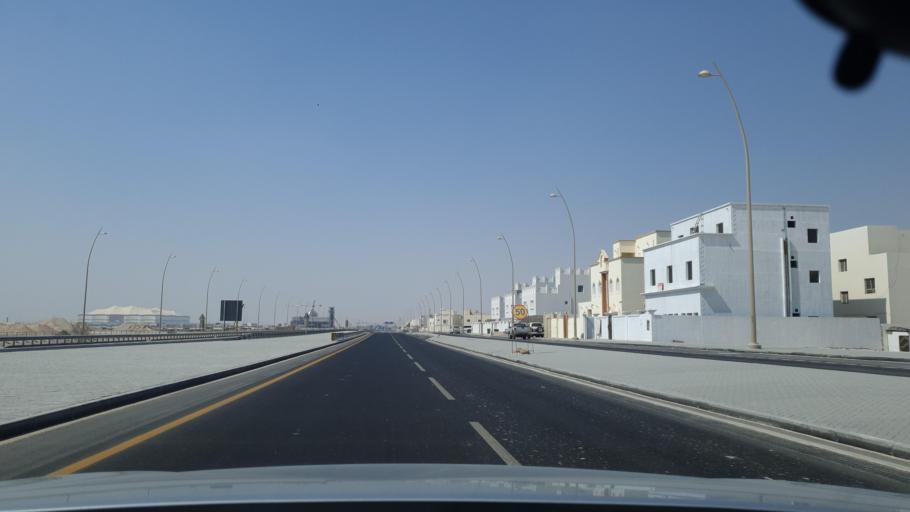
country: QA
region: Al Khawr
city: Al Khawr
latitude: 25.6663
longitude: 51.5147
